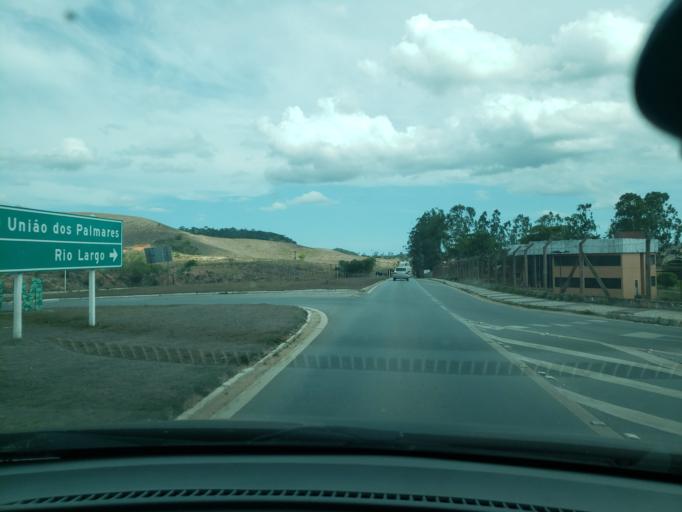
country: BR
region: Alagoas
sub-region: Murici
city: Murici
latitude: -9.3124
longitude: -35.9339
